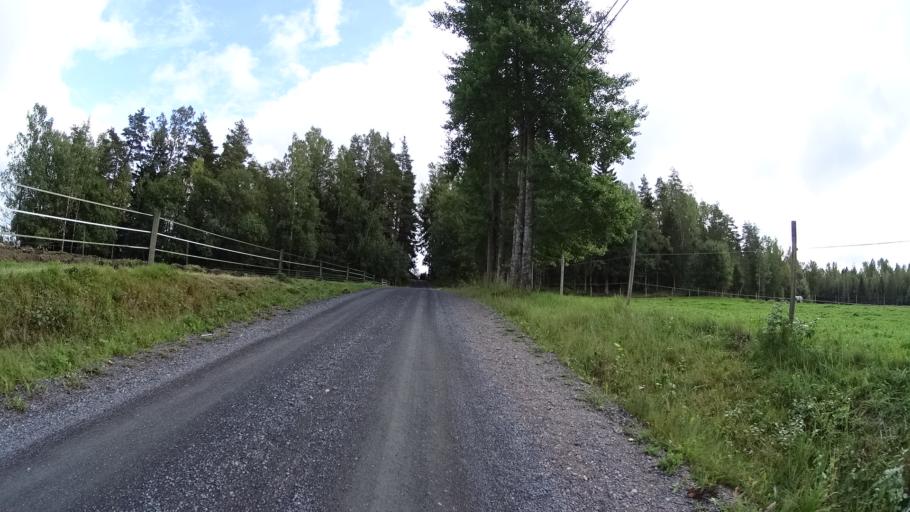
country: FI
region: Uusimaa
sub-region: Helsinki
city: Espoo
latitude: 60.2368
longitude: 24.6455
